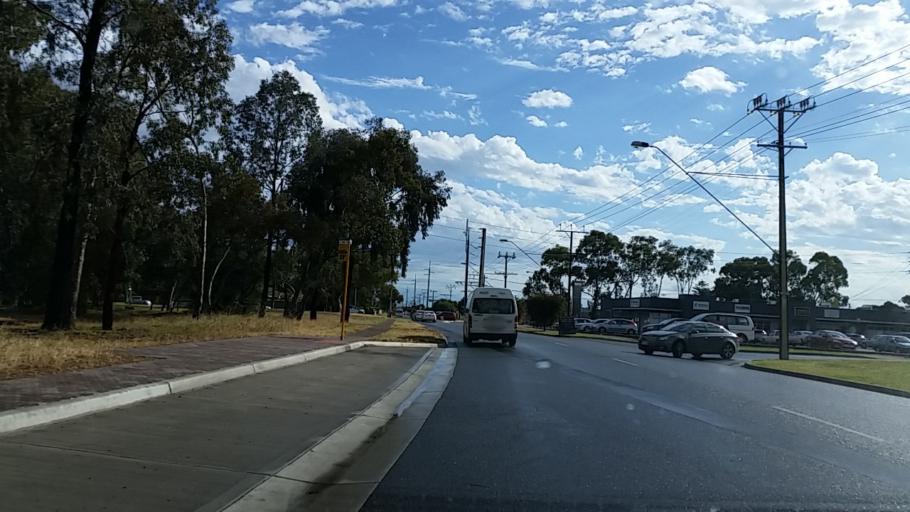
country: AU
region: South Australia
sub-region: Salisbury
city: Salisbury
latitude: -34.7809
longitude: 138.6091
